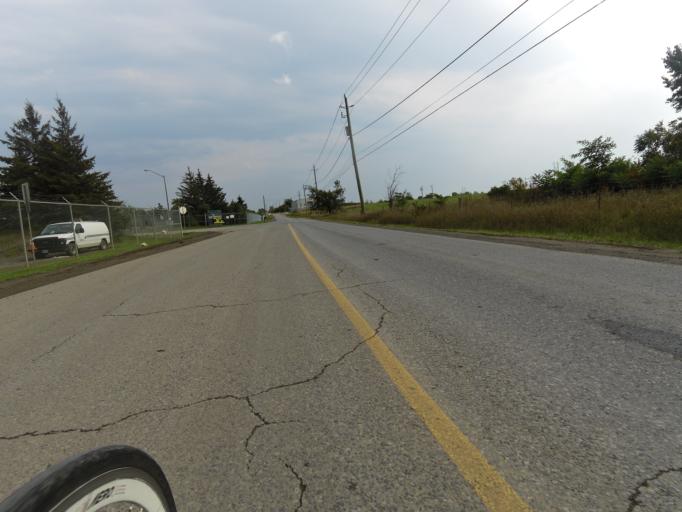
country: CA
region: Ontario
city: Bells Corners
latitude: 45.2339
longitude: -75.7744
